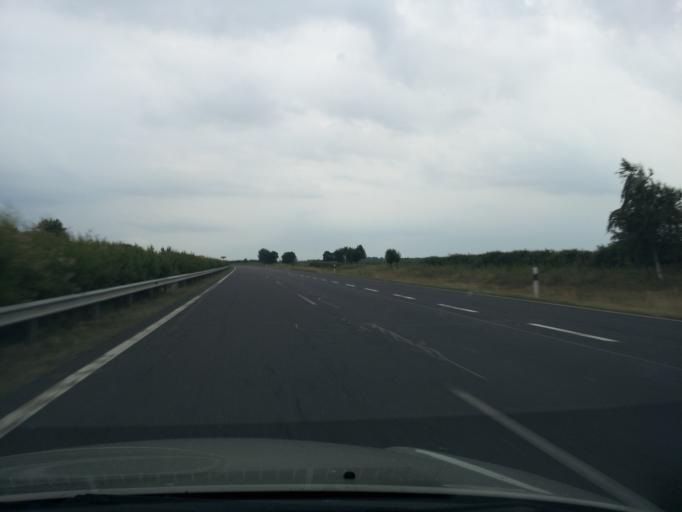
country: HU
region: Borsod-Abauj-Zemplen
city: Emod
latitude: 47.9161
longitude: 20.8432
